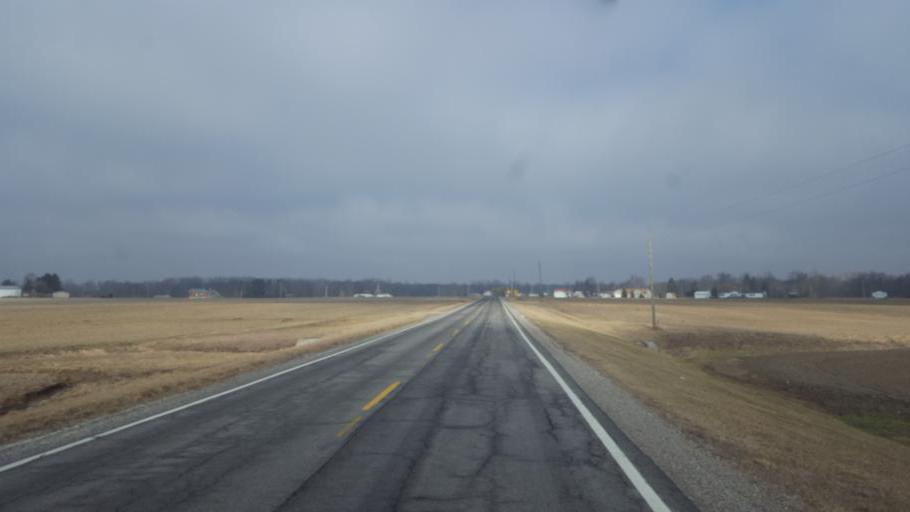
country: US
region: Ohio
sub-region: Crawford County
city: Bucyrus
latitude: 40.7371
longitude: -82.8989
